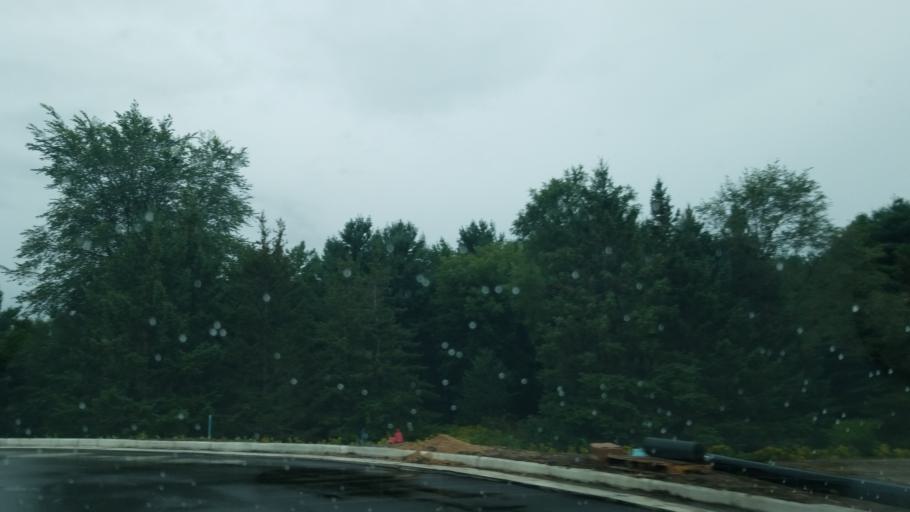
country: US
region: Wisconsin
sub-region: Saint Croix County
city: Hudson
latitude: 44.9745
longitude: -92.7229
